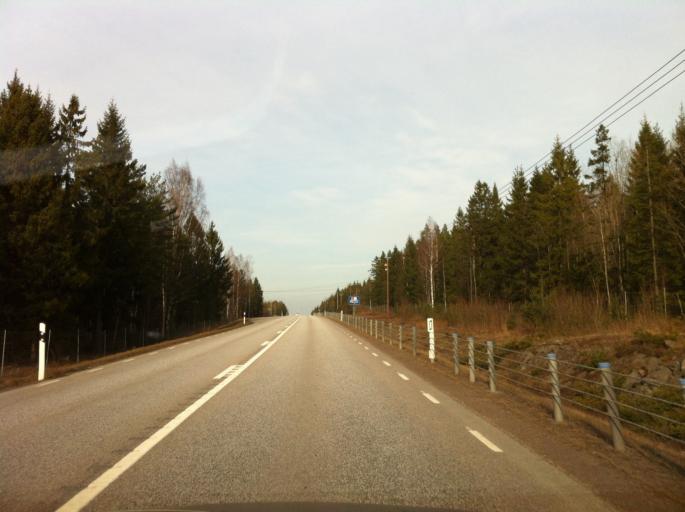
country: SE
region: Vaestra Goetaland
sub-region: Gullspangs Kommun
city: Gullspang
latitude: 58.9491
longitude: 14.0517
